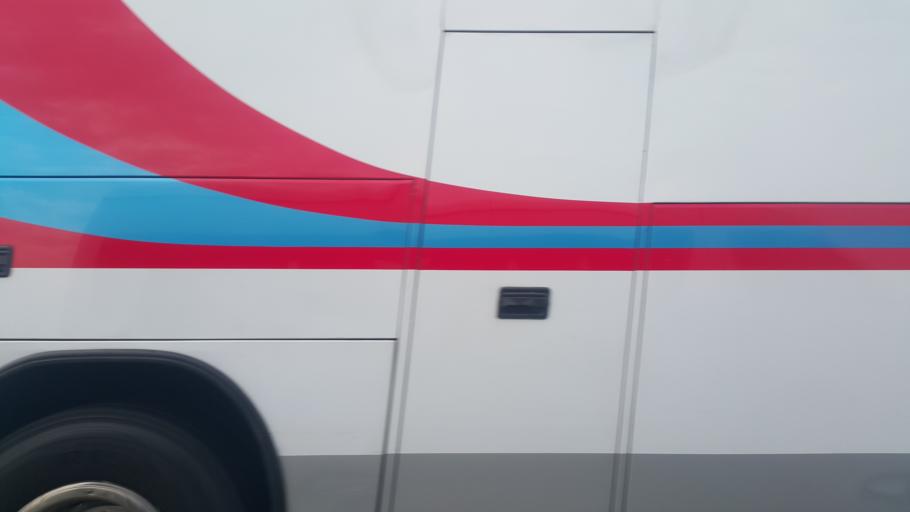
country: MY
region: Johor
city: Johor Bahru
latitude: 1.3566
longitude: 103.6253
